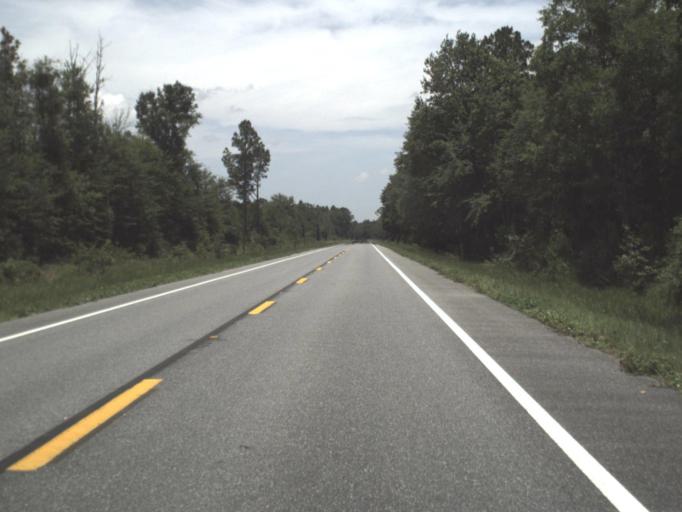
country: US
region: Florida
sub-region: Lafayette County
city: Mayo
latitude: 30.0011
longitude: -83.1944
